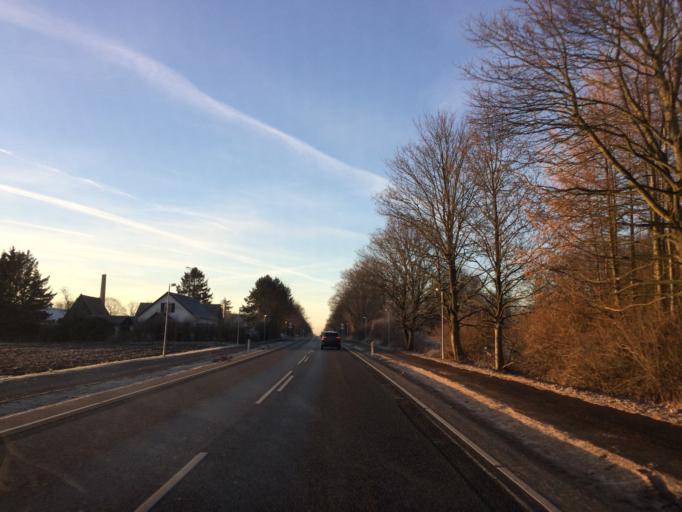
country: DK
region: South Denmark
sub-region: Odense Kommune
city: Bellinge
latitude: 55.3286
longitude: 10.3271
